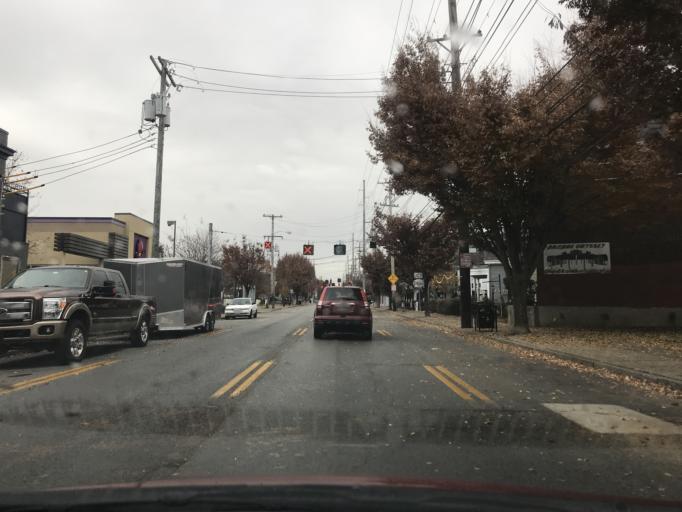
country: US
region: Kentucky
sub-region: Jefferson County
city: Audubon Park
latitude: 38.2392
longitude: -85.7224
